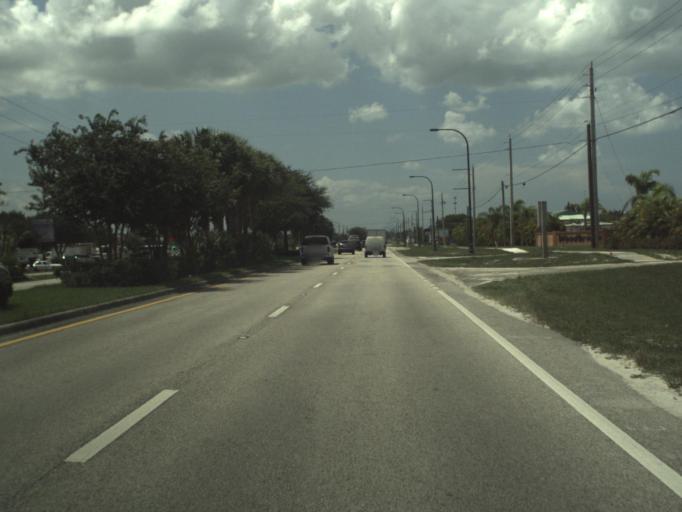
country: US
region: Florida
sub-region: Martin County
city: Hobe Sound
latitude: 27.0686
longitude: -80.1405
